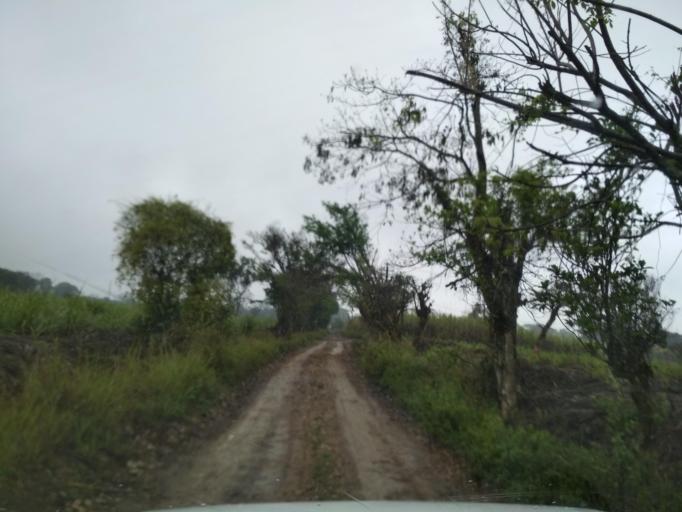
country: MX
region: Veracruz
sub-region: Amatlan de los Reyes
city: Centro de Readaptacion Social
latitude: 18.8252
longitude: -96.9385
